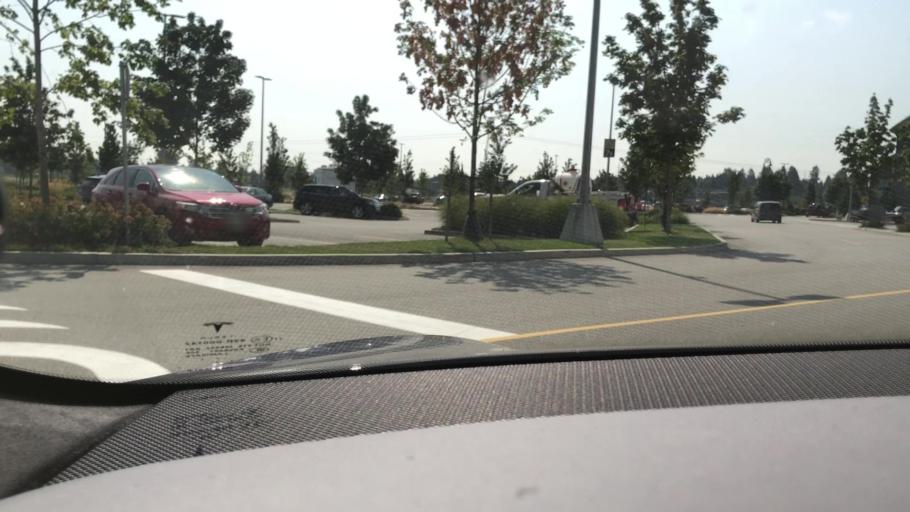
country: CA
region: British Columbia
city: Ladner
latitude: 49.0403
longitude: -123.0819
